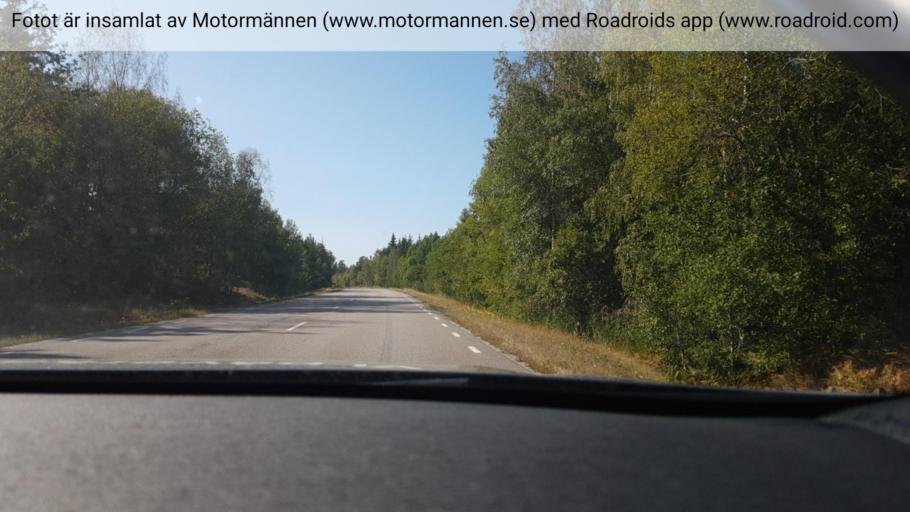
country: SE
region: Vaestra Goetaland
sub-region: Gotene Kommun
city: Goetene
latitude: 58.6218
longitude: 13.4782
